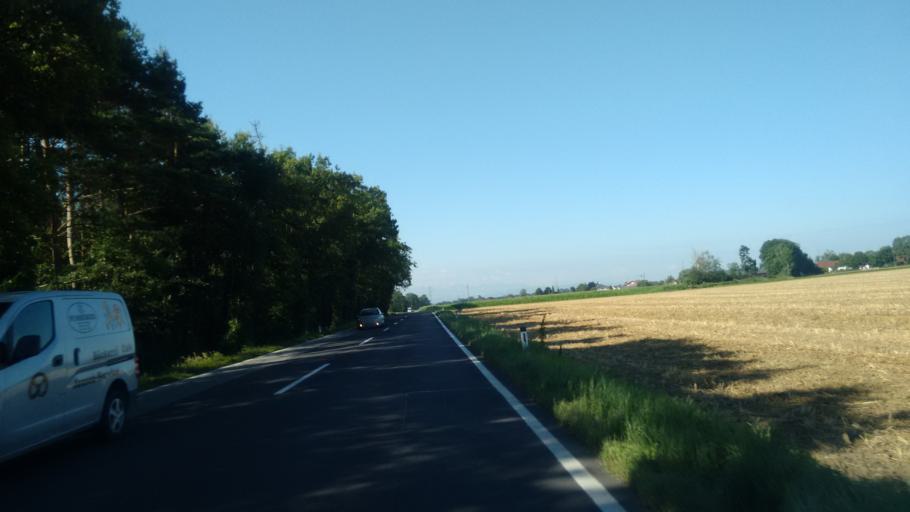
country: AT
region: Upper Austria
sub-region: Wels-Land
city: Gunskirchen
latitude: 48.1149
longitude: 13.9341
